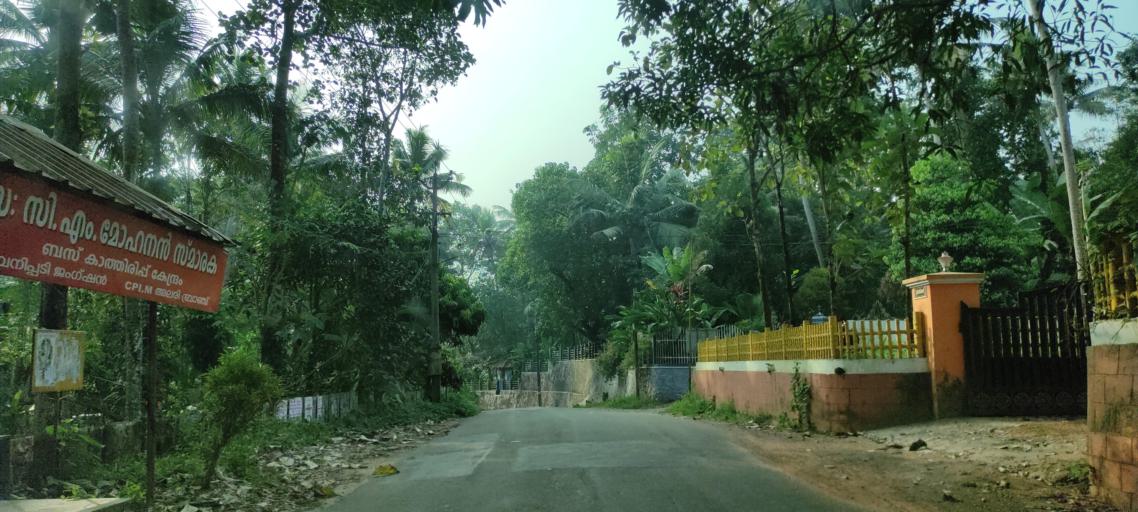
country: IN
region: Kerala
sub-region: Ernakulam
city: Piravam
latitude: 9.7756
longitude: 76.4946
